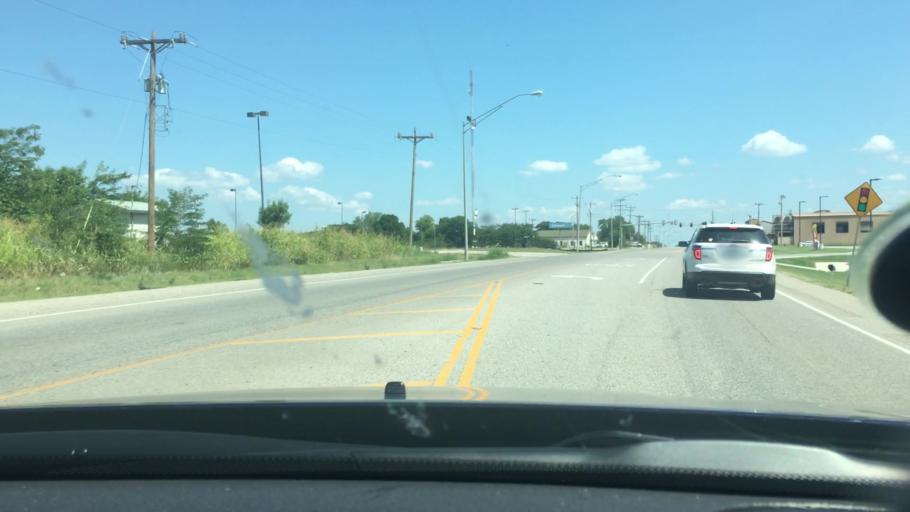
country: US
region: Oklahoma
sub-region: Marshall County
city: Madill
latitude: 34.0685
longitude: -96.7633
